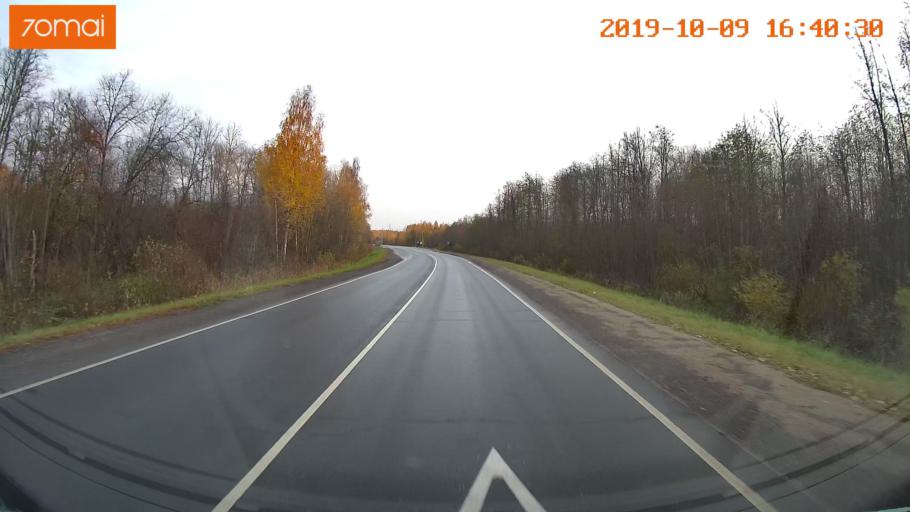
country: RU
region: Kostroma
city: Volgorechensk
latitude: 57.4829
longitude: 41.0617
